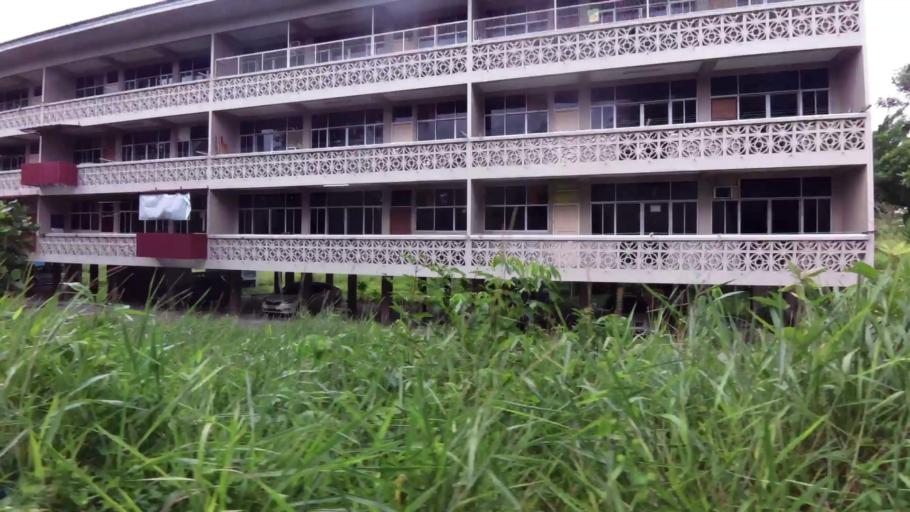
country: BN
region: Brunei and Muara
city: Bandar Seri Begawan
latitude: 4.9470
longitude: 114.9557
